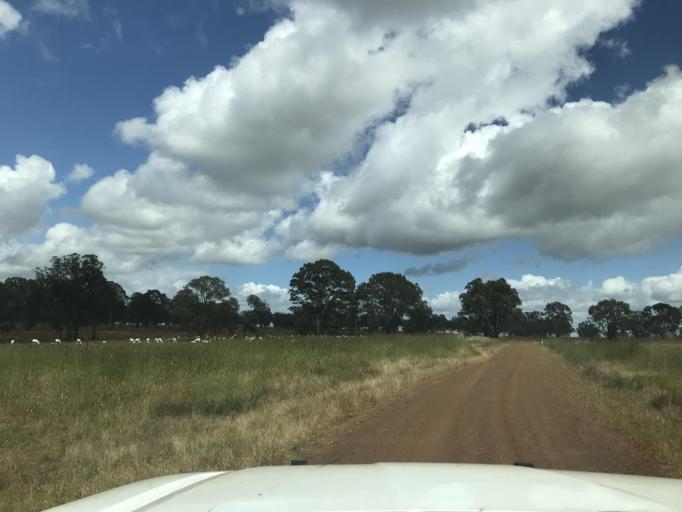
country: AU
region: South Australia
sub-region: Wattle Range
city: Penola
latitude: -37.1958
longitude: 141.4314
